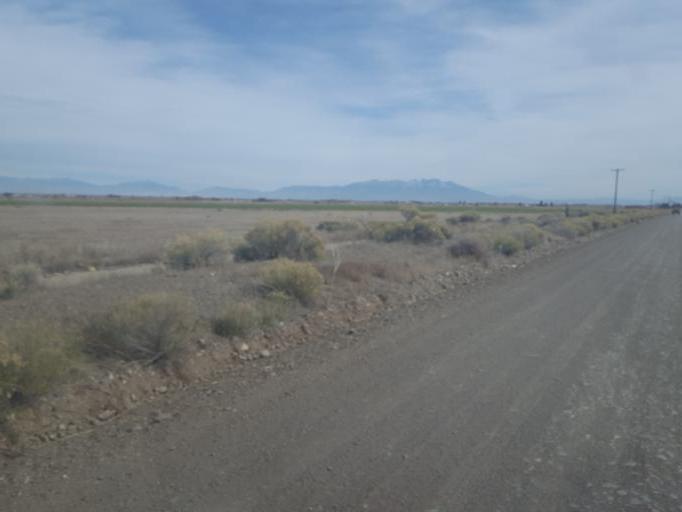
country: US
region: Colorado
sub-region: Rio Grande County
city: Monte Vista
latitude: 37.4011
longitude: -106.1032
